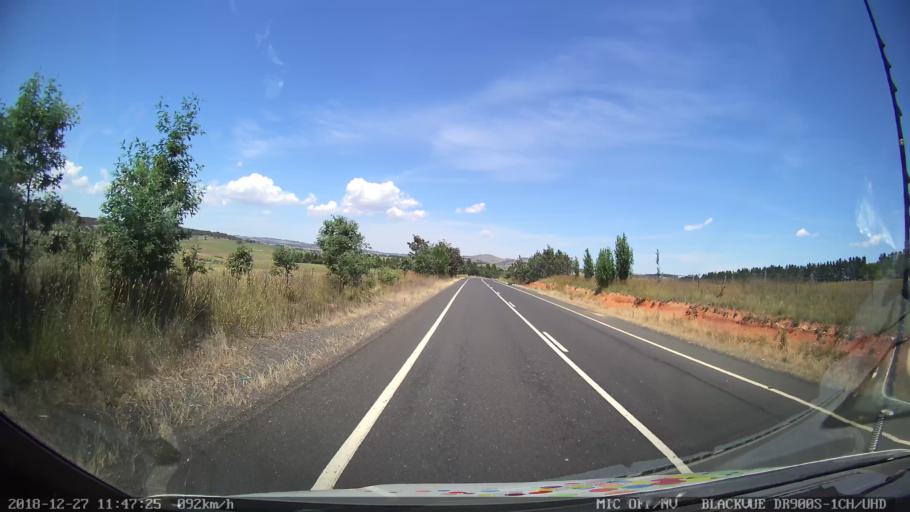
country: AU
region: New South Wales
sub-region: Bathurst Regional
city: Perthville
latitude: -33.5962
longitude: 149.4455
